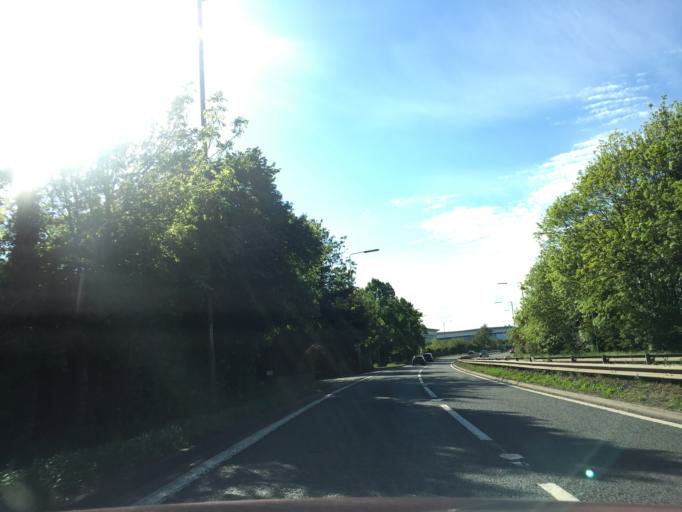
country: GB
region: England
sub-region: Warwickshire
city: Ryton on Dunsmore
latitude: 52.3668
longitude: -1.4389
